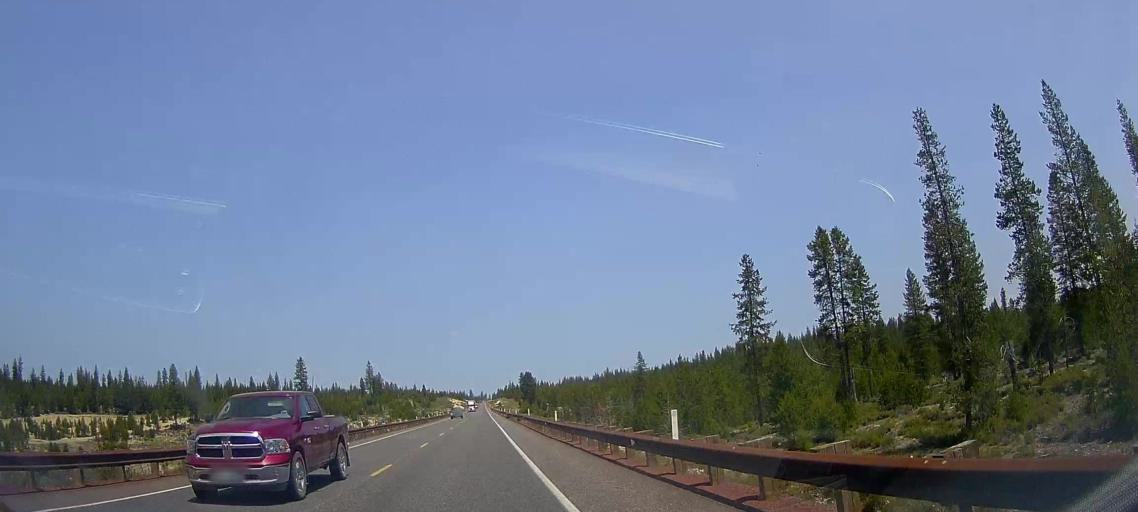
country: US
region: Oregon
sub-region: Deschutes County
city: La Pine
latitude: 43.3978
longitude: -121.7258
